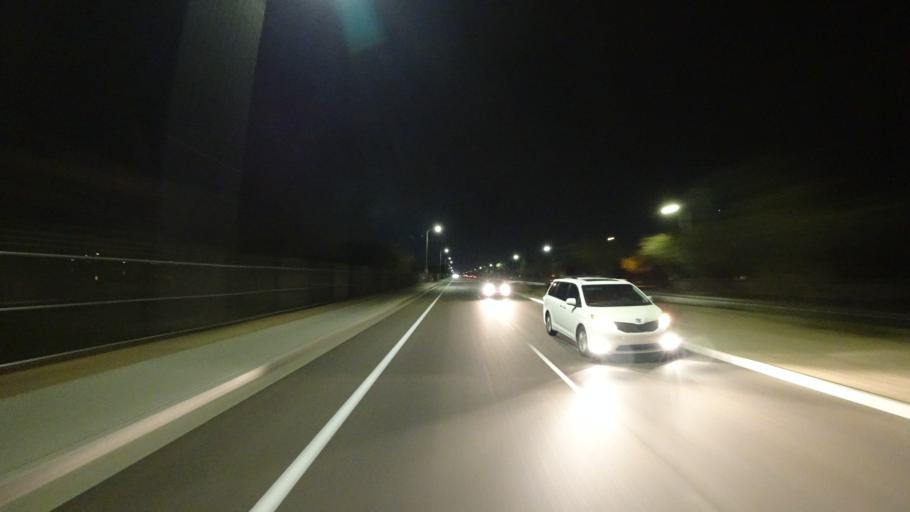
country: US
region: Arizona
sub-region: Maricopa County
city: Sun Lakes
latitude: 33.2241
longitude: -111.7894
